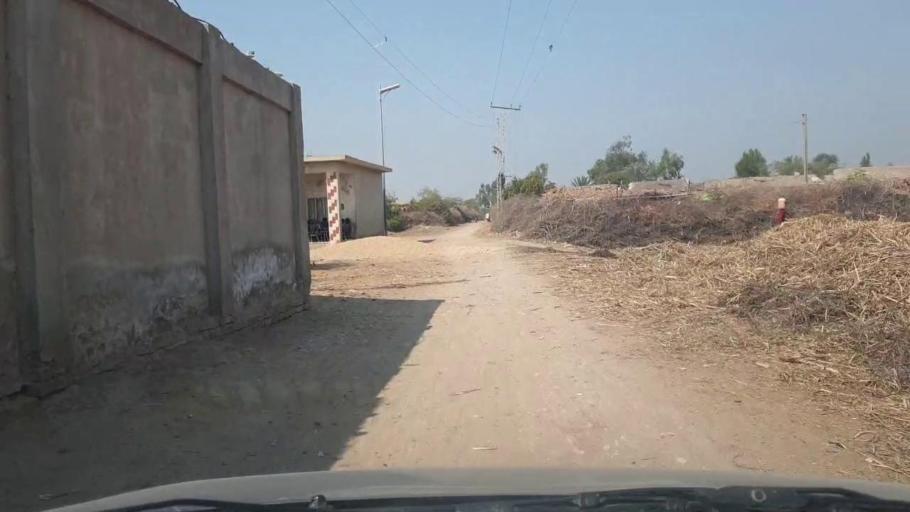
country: PK
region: Sindh
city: Mirwah Gorchani
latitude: 25.3556
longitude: 69.1463
